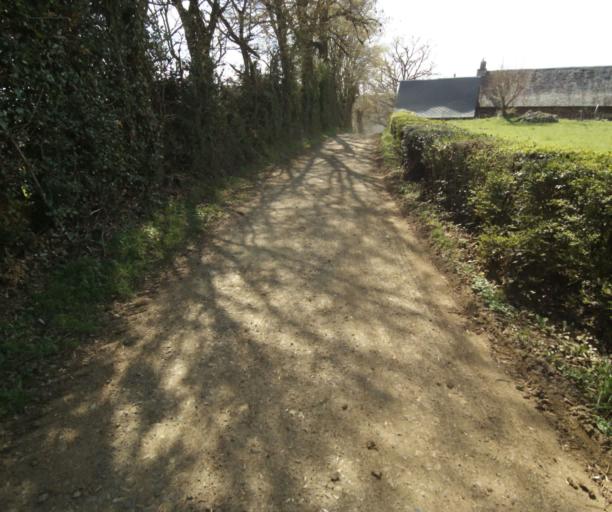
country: FR
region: Limousin
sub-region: Departement de la Correze
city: Naves
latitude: 45.3695
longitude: 1.7755
